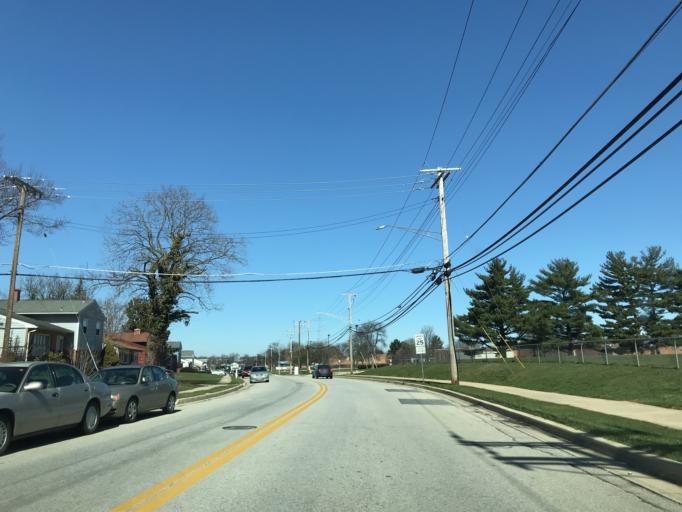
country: US
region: Maryland
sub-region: Baltimore County
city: Catonsville
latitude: 39.2976
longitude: -76.7352
